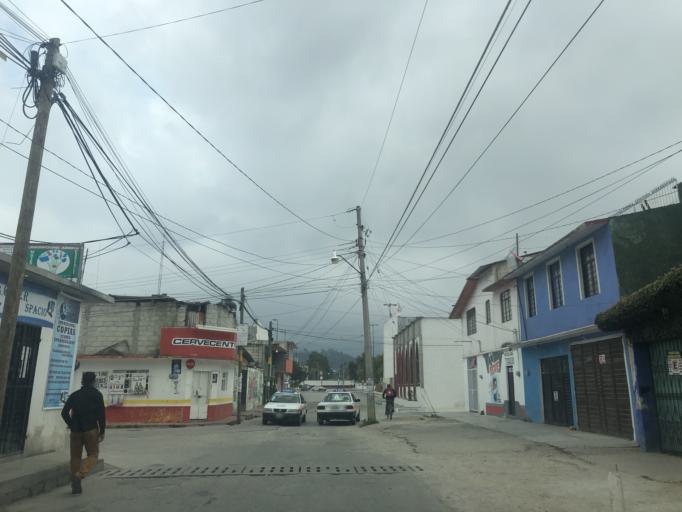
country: MX
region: Chiapas
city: San Cristobal de las Casas
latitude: 16.7195
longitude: -92.6431
